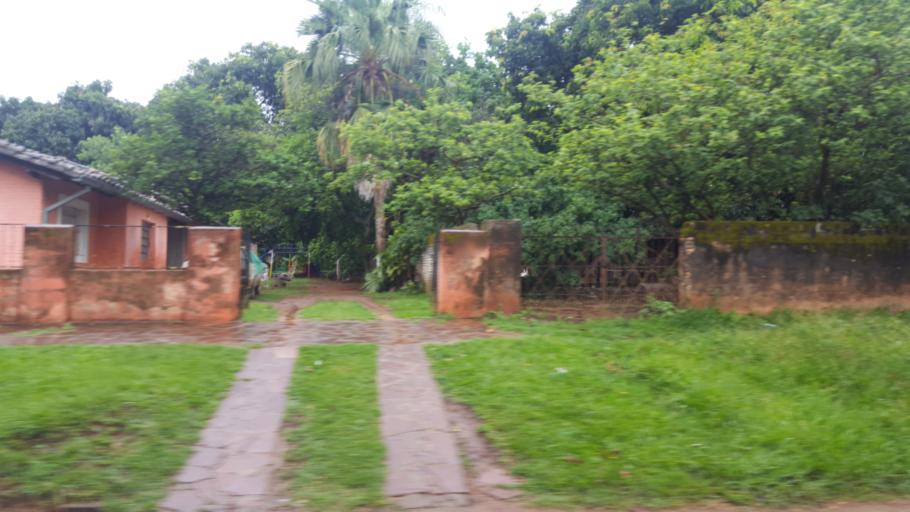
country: PY
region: Misiones
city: San Juan Bautista
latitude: -26.6701
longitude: -57.1490
